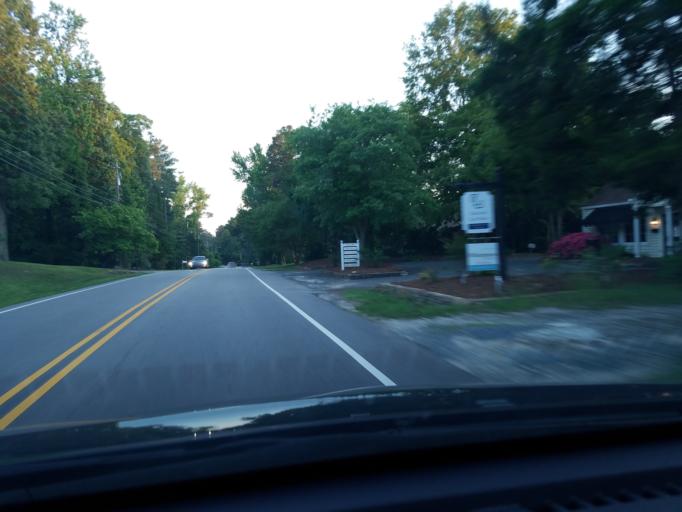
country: US
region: North Carolina
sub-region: Durham County
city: Durham
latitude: 35.9640
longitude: -78.9327
